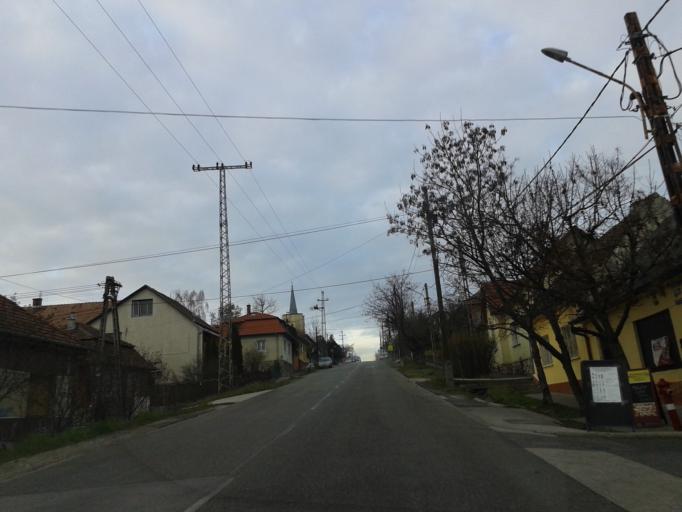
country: HU
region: Budapest
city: Budapest XXII. keruelet
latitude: 47.4047
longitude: 19.0005
